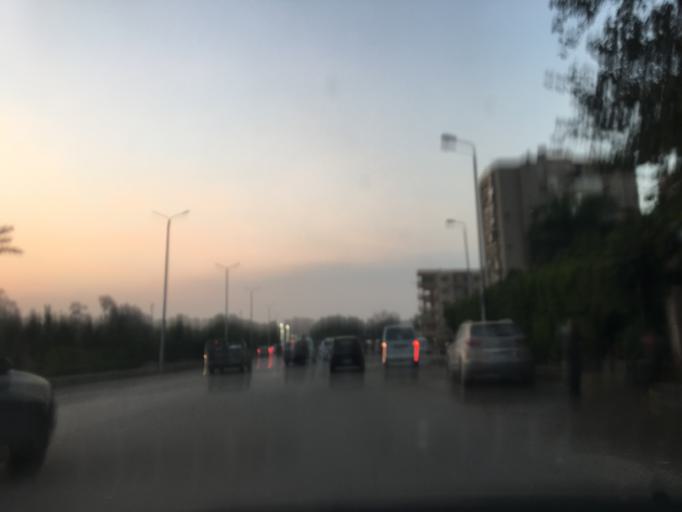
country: EG
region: Al Jizah
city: Al Jizah
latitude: 29.9898
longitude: 31.1356
